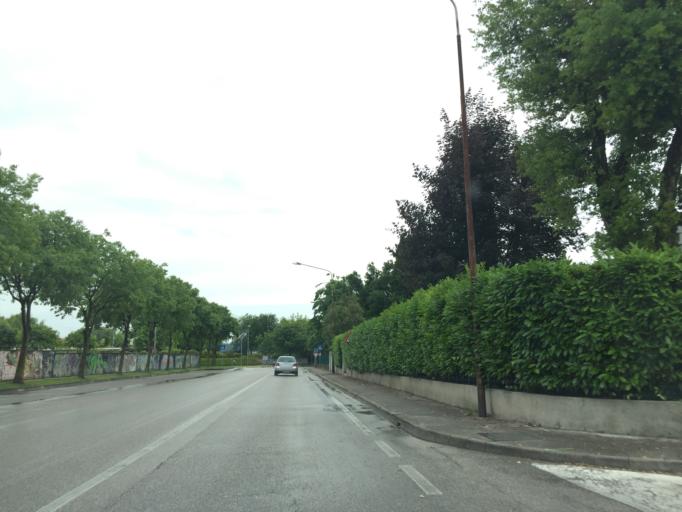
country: IT
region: Friuli Venezia Giulia
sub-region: Provincia di Pordenone
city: Porcia
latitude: 45.9579
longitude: 12.6083
